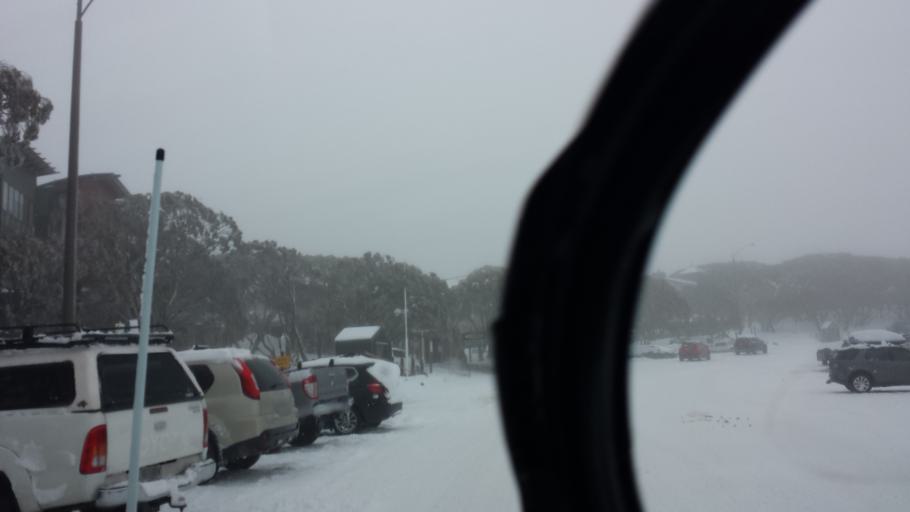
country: AU
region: Victoria
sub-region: Alpine
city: Mount Beauty
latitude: -36.9938
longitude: 147.1519
